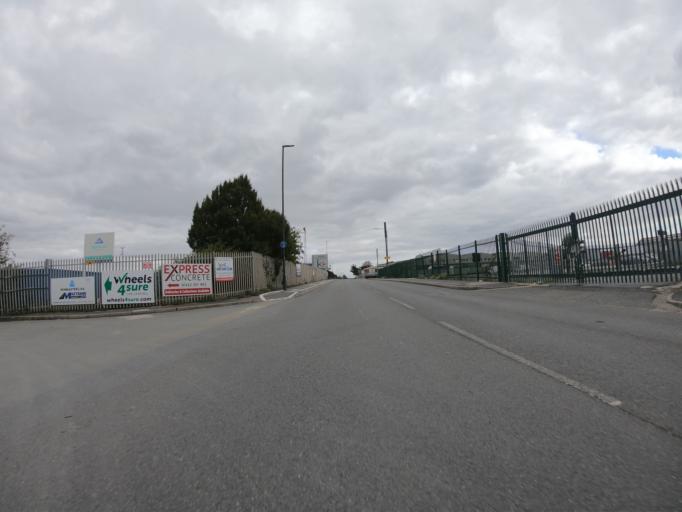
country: GB
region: England
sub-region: Greater London
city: Erith
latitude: 51.4773
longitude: 0.1941
